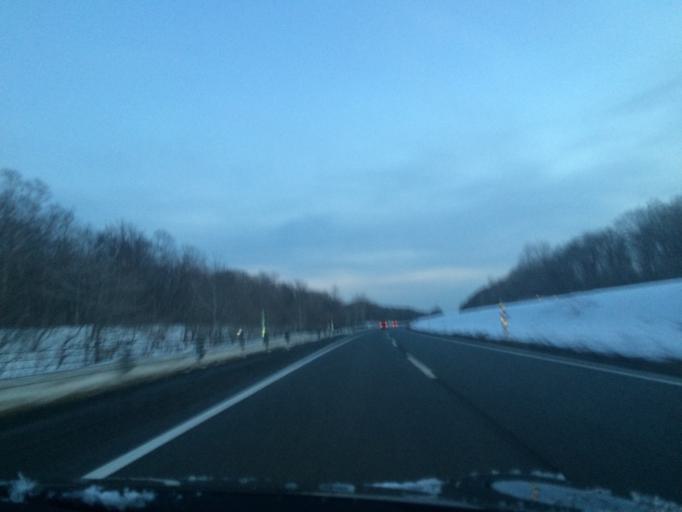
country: JP
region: Hokkaido
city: Chitose
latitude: 42.7971
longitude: 141.6267
